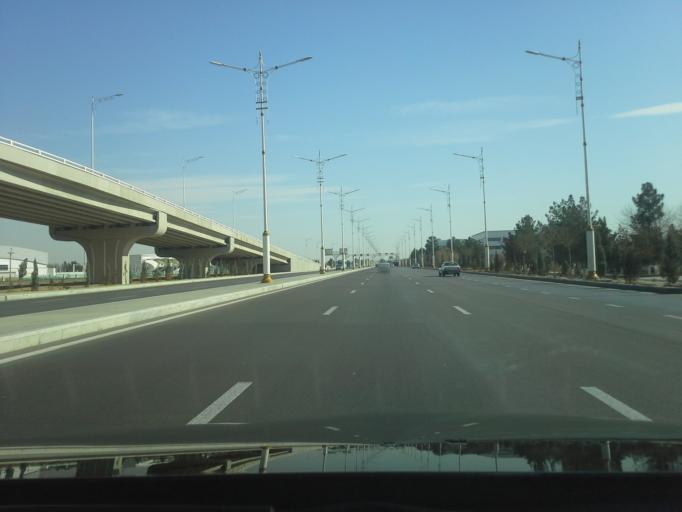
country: TM
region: Ahal
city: Ashgabat
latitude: 37.9253
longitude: 58.4333
